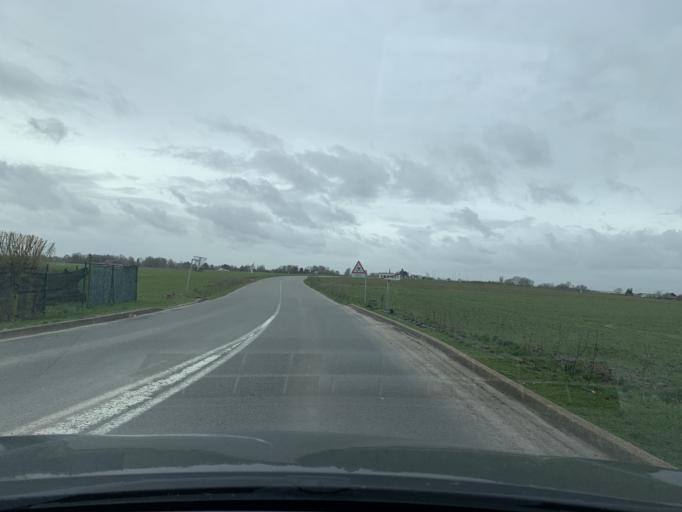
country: FR
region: Nord-Pas-de-Calais
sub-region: Departement du Nord
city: Cambrai
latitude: 50.1551
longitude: 3.2718
